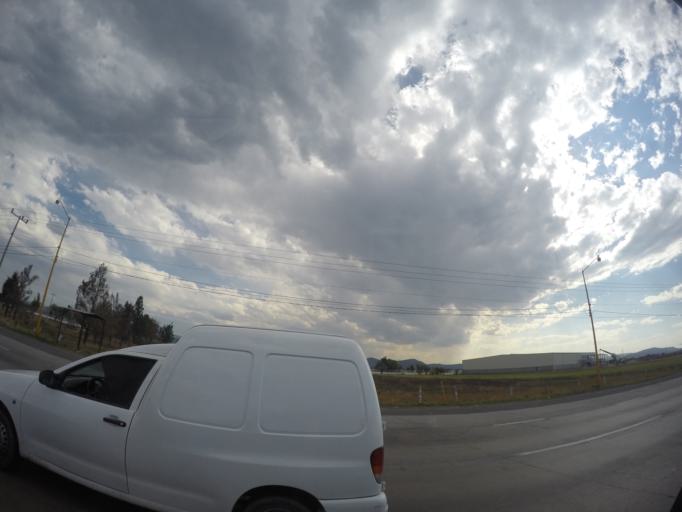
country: MX
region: Queretaro
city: La Estancia
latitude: 20.4314
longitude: -100.0622
